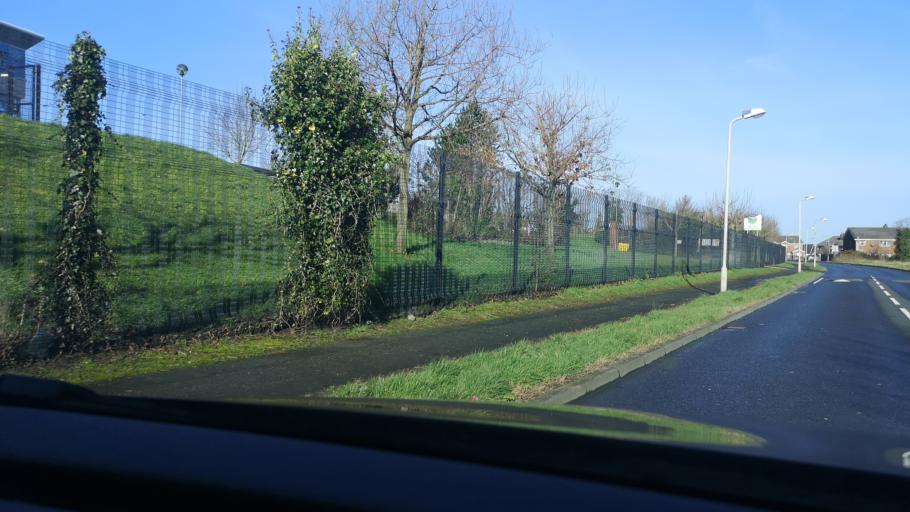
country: GB
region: Northern Ireland
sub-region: Newry and Mourne District
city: Newry
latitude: 54.1773
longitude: -6.3533
